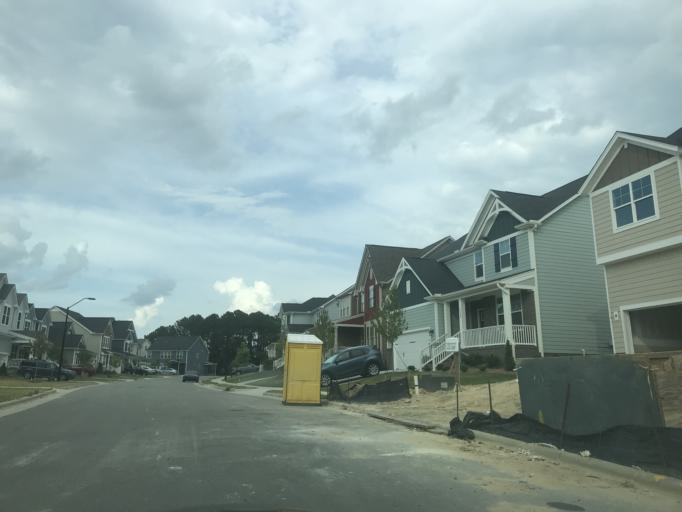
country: US
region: North Carolina
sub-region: Wake County
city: Knightdale
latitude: 35.8385
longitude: -78.5553
